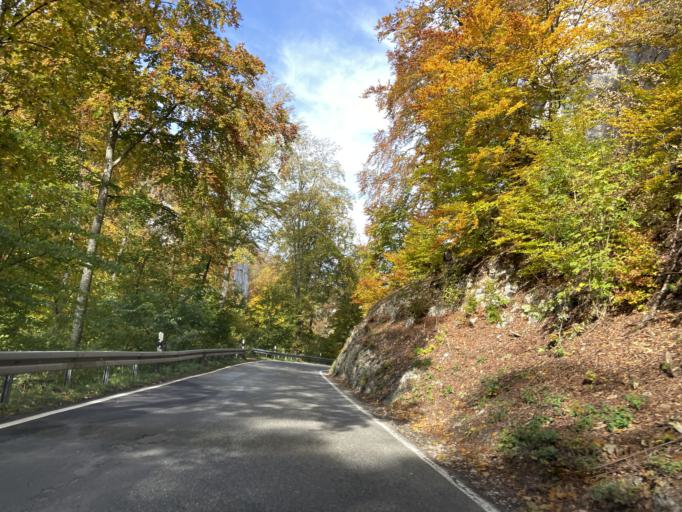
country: DE
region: Baden-Wuerttemberg
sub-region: Tuebingen Region
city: Leibertingen
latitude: 48.0674
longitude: 9.0357
